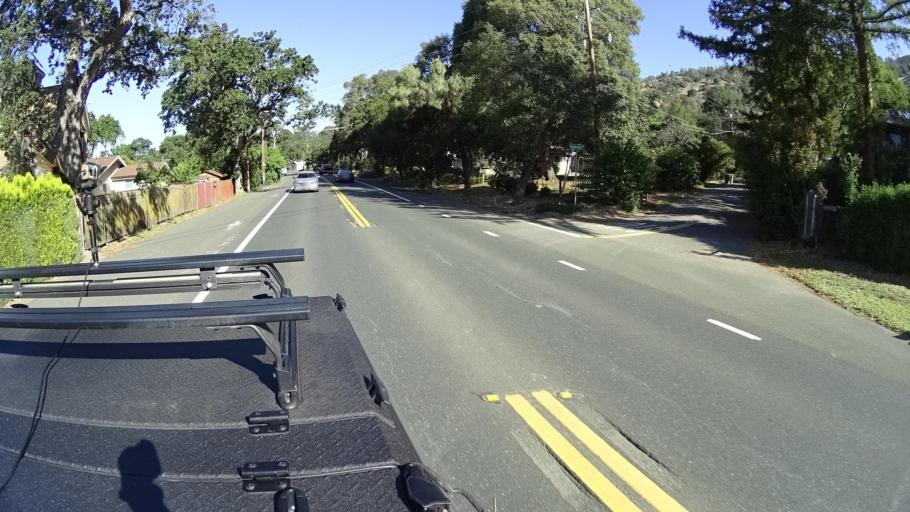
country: US
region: California
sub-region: Lake County
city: Clearlake Oaks
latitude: 39.0212
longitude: -122.7109
